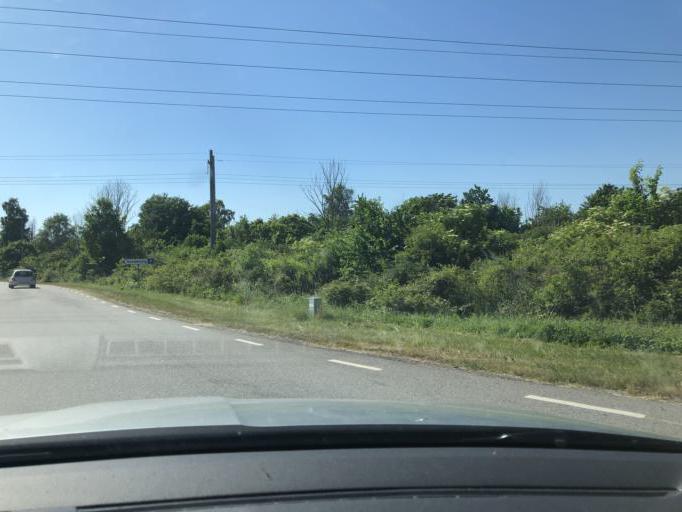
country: SE
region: Skane
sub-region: Bromolla Kommun
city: Bromoella
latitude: 56.0763
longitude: 14.4989
